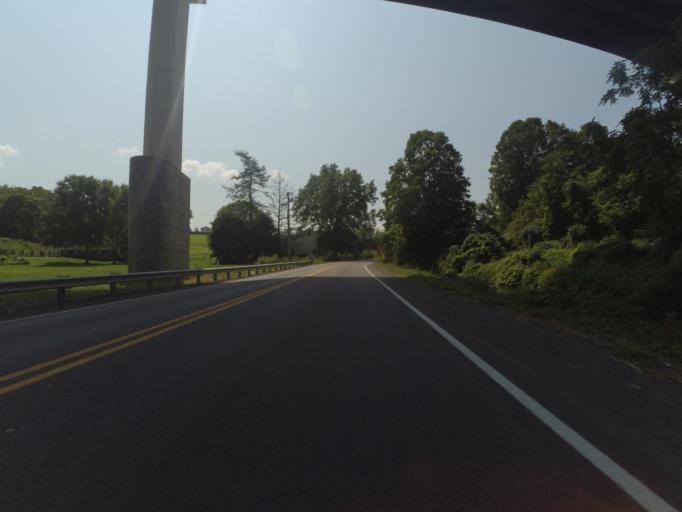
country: US
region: Pennsylvania
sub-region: Centre County
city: Pleasant Gap
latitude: 40.8810
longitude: -77.7613
